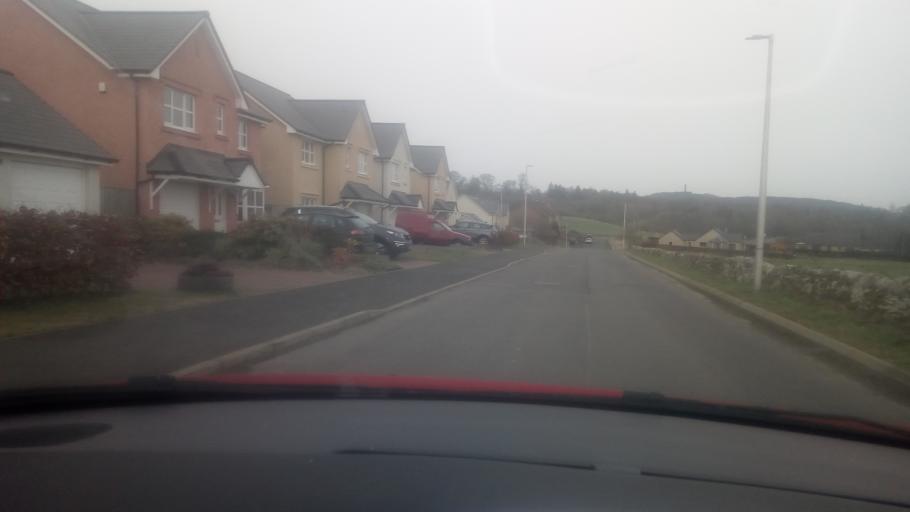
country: GB
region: Scotland
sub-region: The Scottish Borders
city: Jedburgh
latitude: 55.5113
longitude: -2.5883
